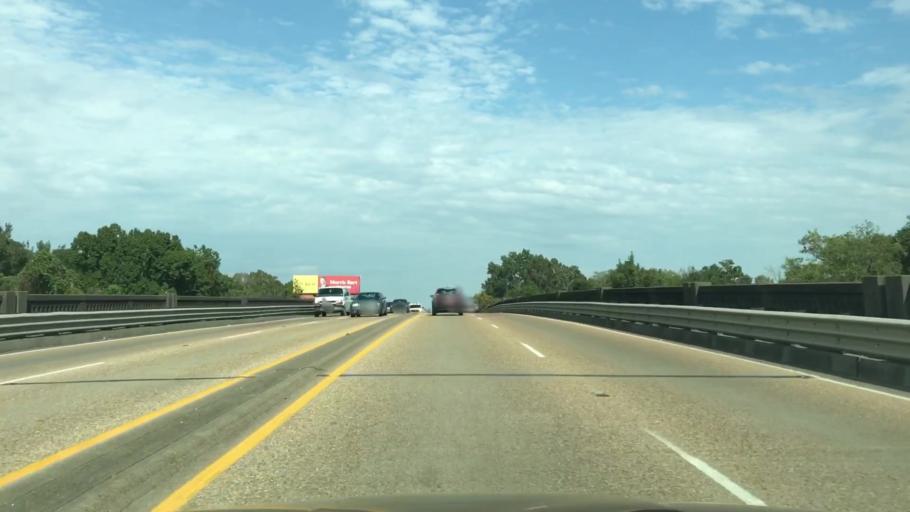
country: US
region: Louisiana
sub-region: Jefferson Parish
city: Bridge City
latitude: 29.9151
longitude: -90.1740
